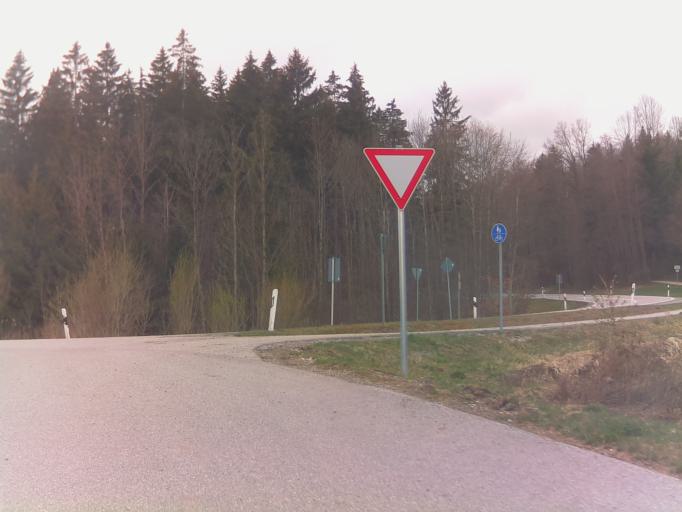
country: DE
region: Bavaria
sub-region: Upper Bavaria
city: Hohenpeissenberg
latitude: 47.7874
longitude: 11.0276
